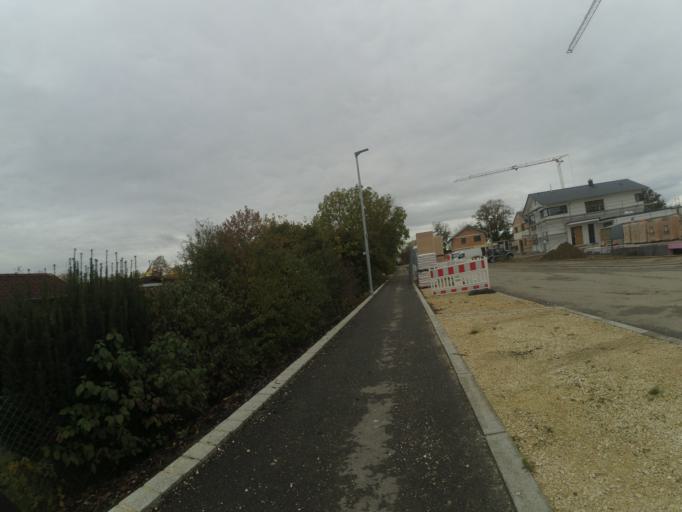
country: DE
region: Bavaria
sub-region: Swabia
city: Neu-Ulm
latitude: 48.3679
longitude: 10.0211
